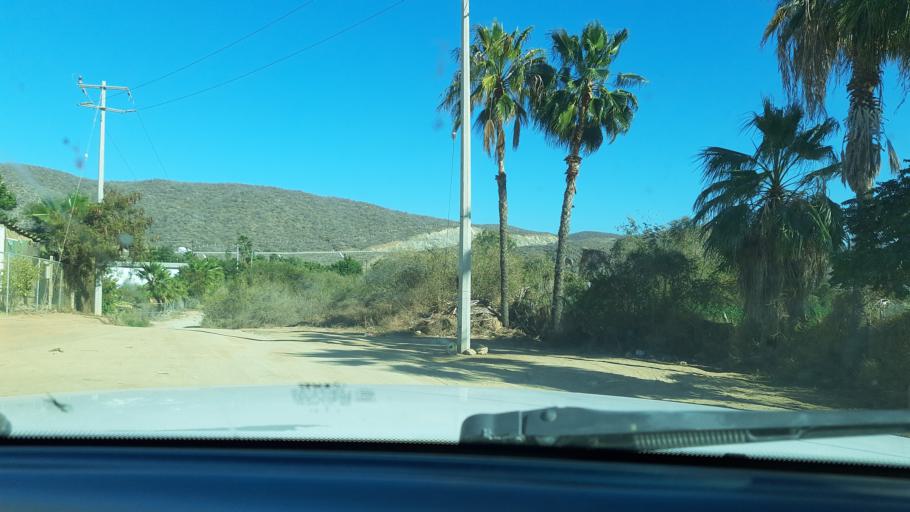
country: MX
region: Baja California Sur
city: Todos Santos
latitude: 23.4738
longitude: -110.2165
